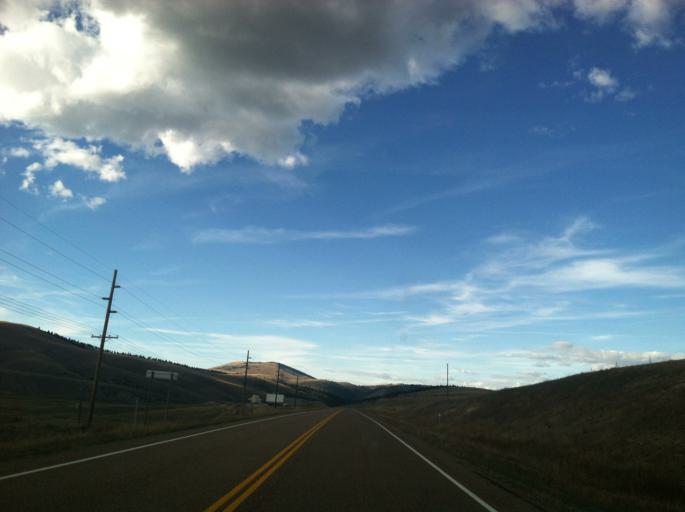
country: US
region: Montana
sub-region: Granite County
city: Philipsburg
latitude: 46.3668
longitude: -113.3141
